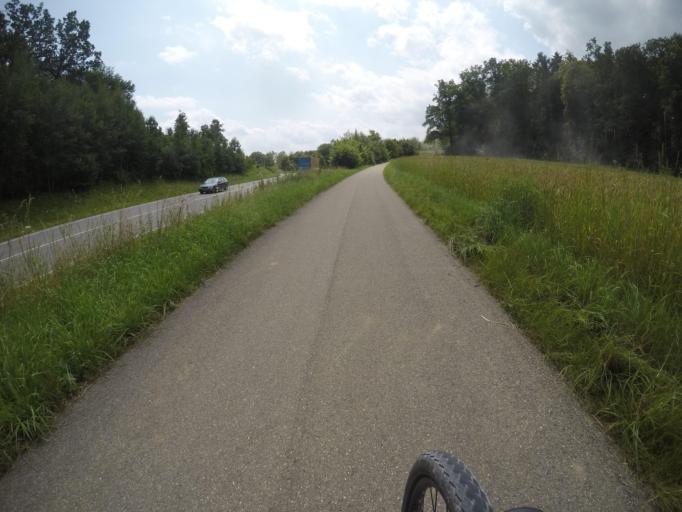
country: DE
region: Baden-Wuerttemberg
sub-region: Freiburg Region
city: Zimmern ob Rottweil
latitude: 48.1819
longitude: 8.6080
